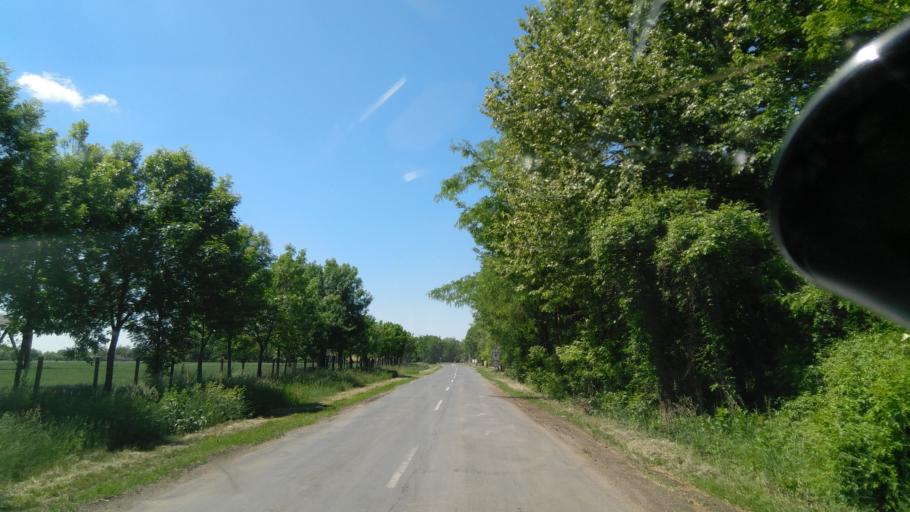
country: HU
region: Bekes
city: Kunagota
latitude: 46.4313
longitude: 21.0616
